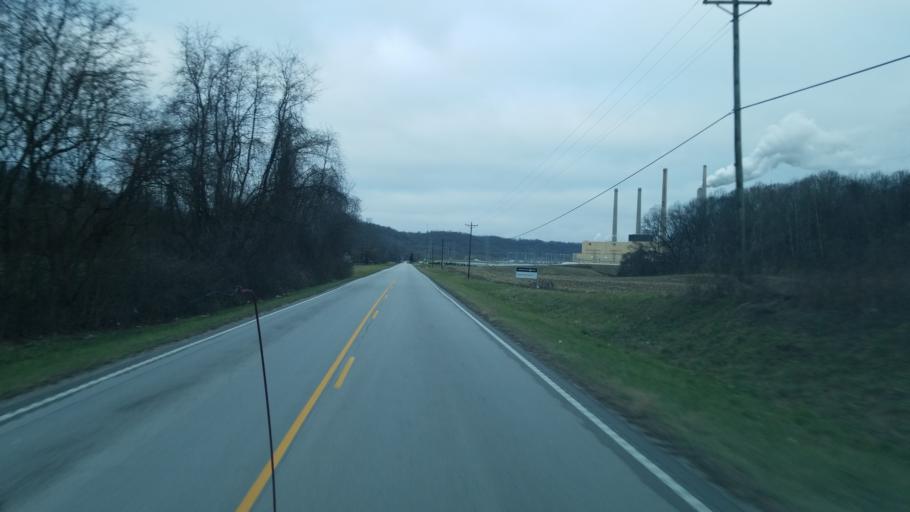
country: US
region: Ohio
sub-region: Brown County
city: Aberdeen
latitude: 38.6897
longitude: -83.8010
